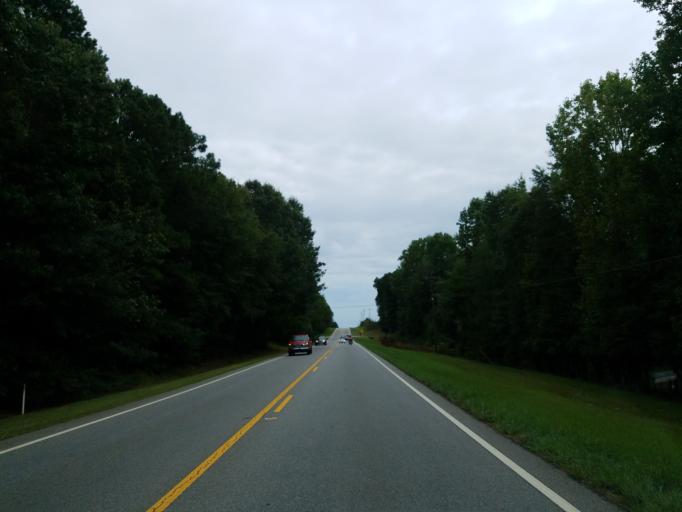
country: US
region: Georgia
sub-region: Lamar County
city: Barnesville
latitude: 33.0207
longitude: -84.1355
